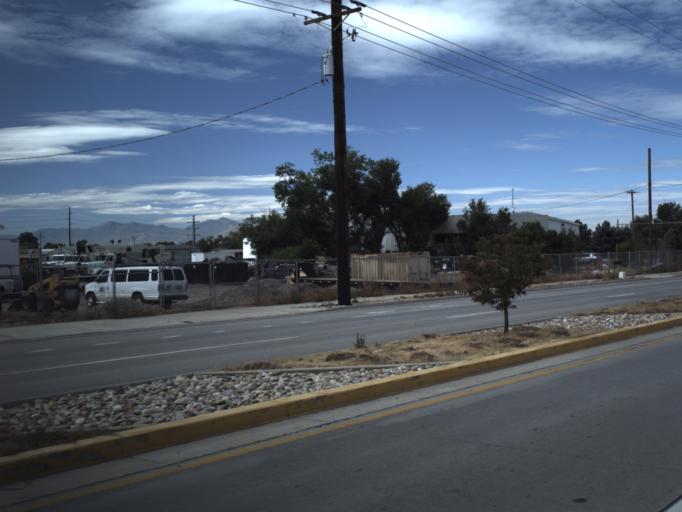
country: US
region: Utah
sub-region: Davis County
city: West Bountiful
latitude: 40.8843
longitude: -111.9067
